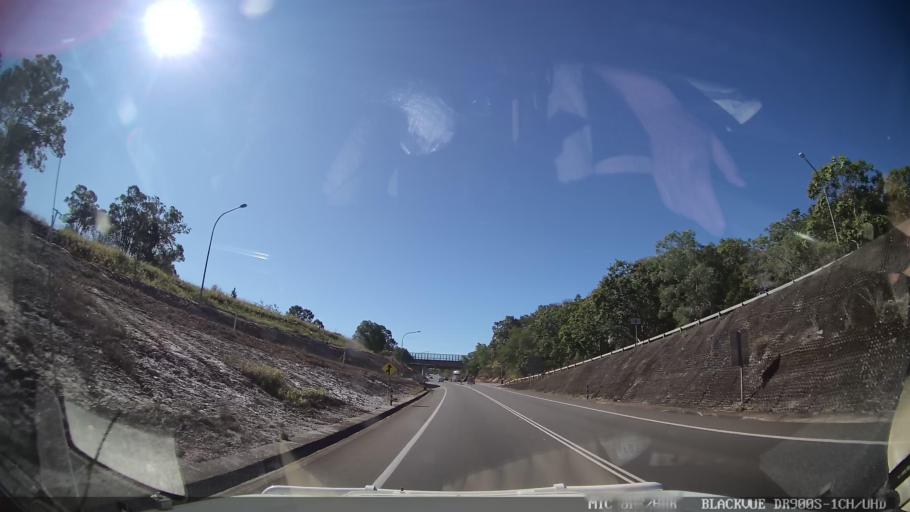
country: AU
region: Queensland
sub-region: Fraser Coast
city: Maryborough
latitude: -25.5189
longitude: 152.6690
